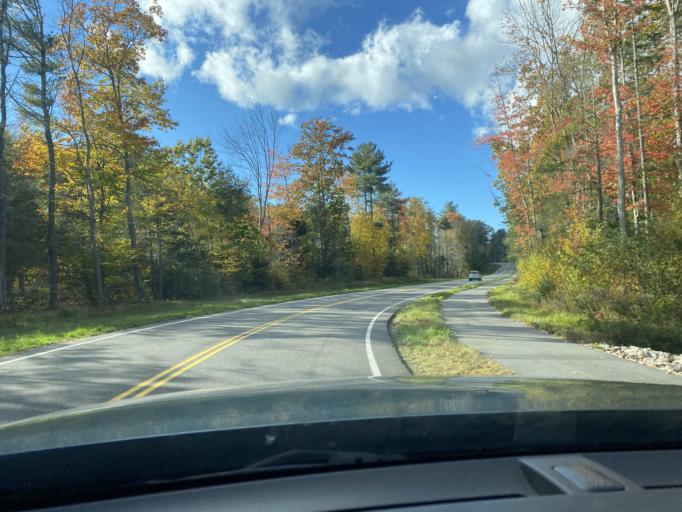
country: US
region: Maine
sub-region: York County
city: York Beach
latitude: 43.1761
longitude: -70.6209
